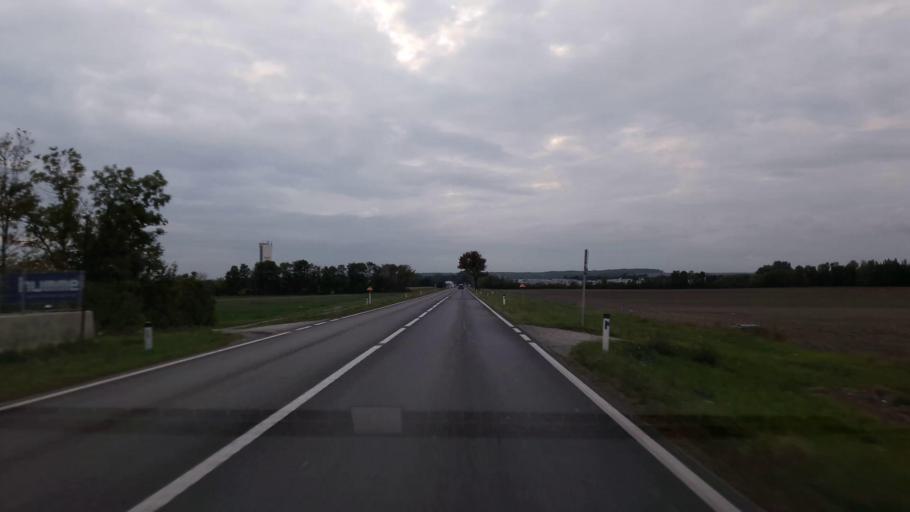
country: AT
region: Lower Austria
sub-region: Politischer Bezirk Bruck an der Leitha
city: Enzersdorf an der Fischa
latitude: 48.0672
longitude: 16.6019
